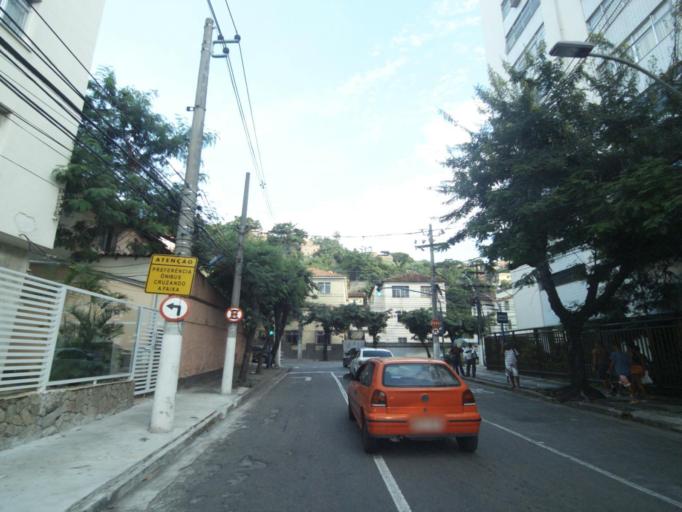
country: BR
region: Rio de Janeiro
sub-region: Niteroi
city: Niteroi
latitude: -22.9106
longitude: -43.1037
